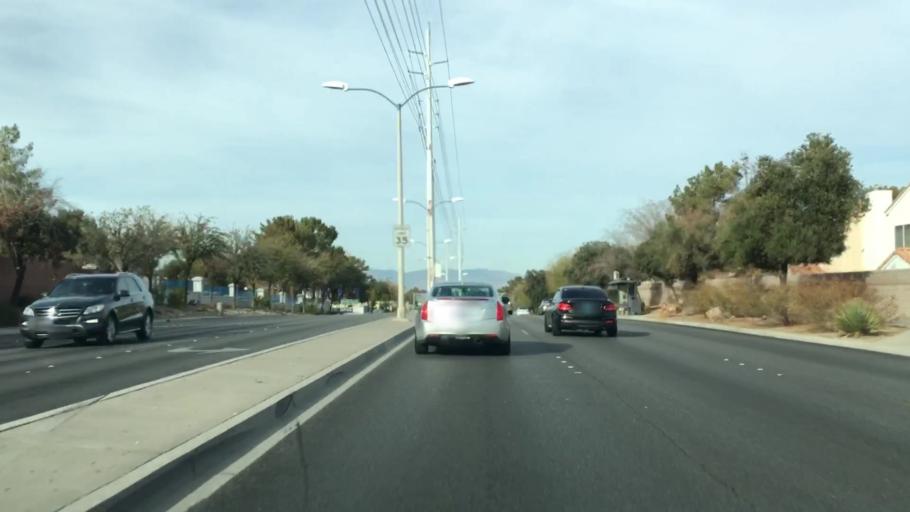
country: US
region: Nevada
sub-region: Clark County
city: Whitney
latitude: 36.0499
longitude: -115.0824
